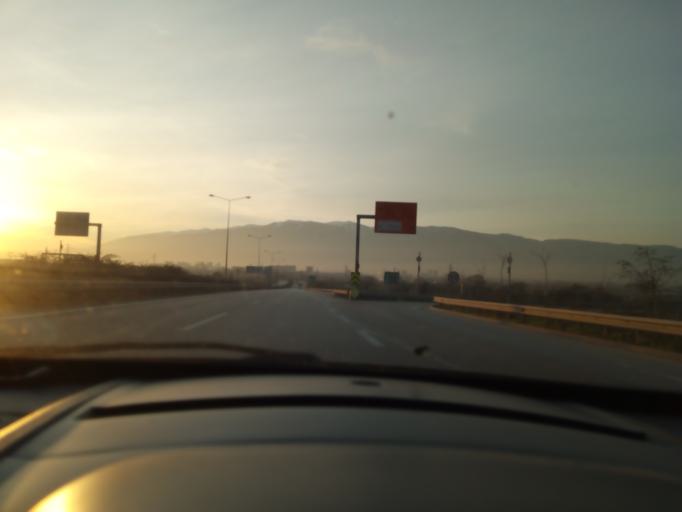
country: TR
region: Bursa
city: Demirtas
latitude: 40.2805
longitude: 29.0419
